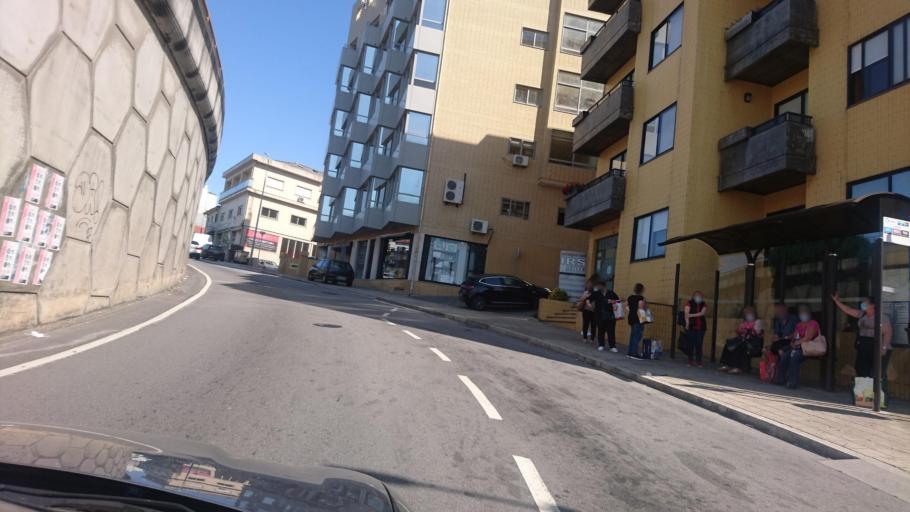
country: PT
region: Porto
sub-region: Gondomar
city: Rio Tinto
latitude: 41.1669
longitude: -8.5667
